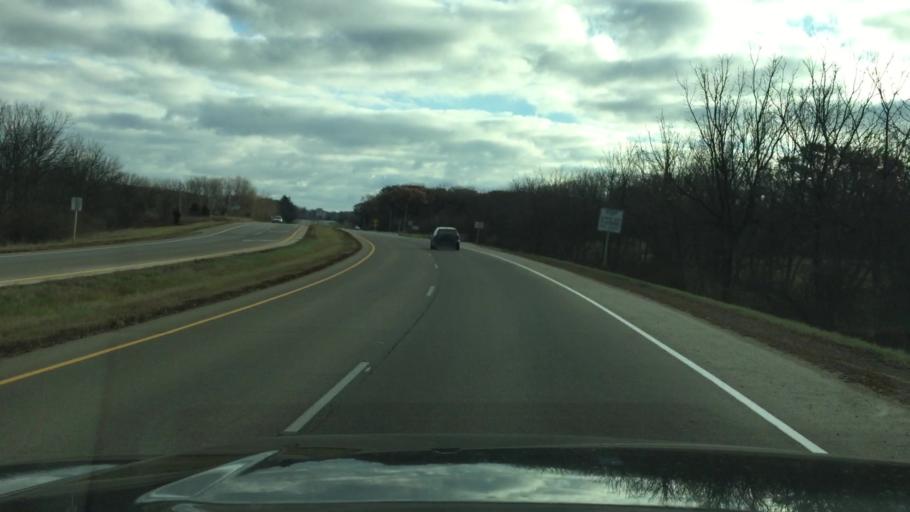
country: US
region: Wisconsin
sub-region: Walworth County
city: Williams Bay
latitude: 42.5828
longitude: -88.5218
